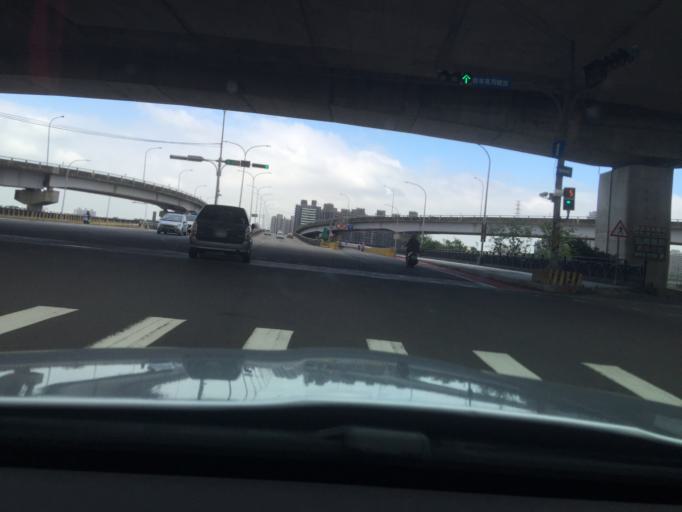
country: TW
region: Taiwan
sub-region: Hsinchu
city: Zhubei
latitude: 24.8194
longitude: 120.9956
